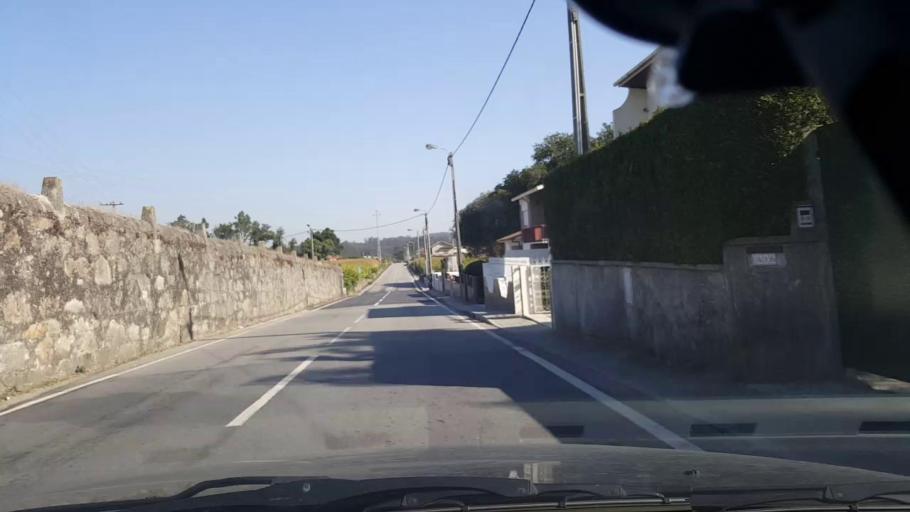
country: PT
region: Porto
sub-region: Vila do Conde
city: Arvore
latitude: 41.3424
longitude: -8.6807
